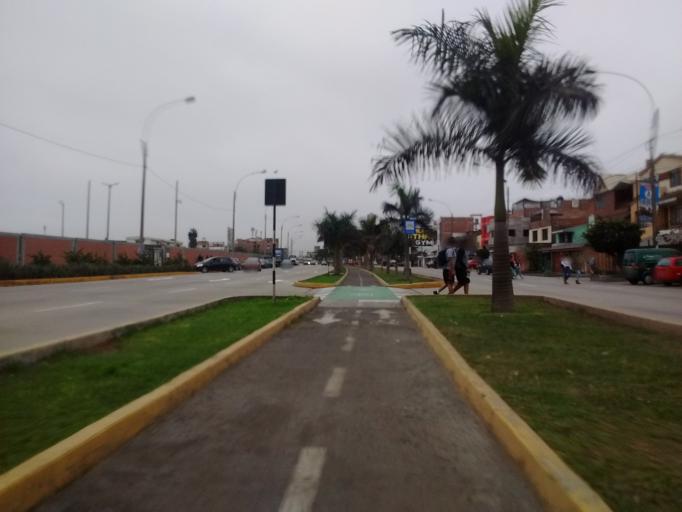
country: PE
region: Callao
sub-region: Callao
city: Callao
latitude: -12.0671
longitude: -77.0778
